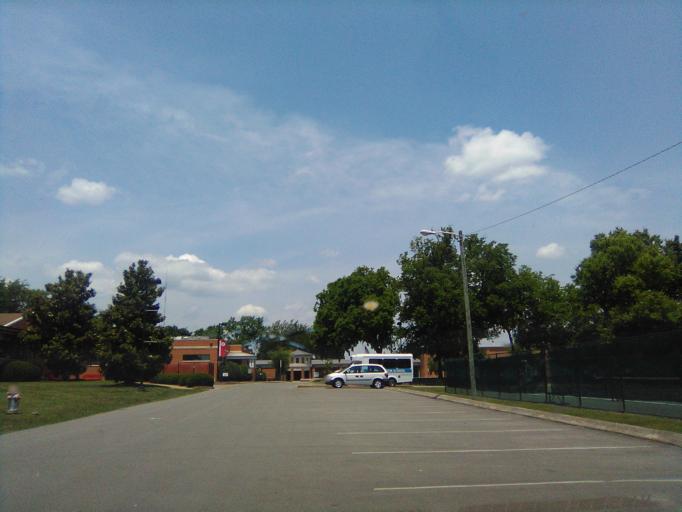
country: US
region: Tennessee
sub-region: Davidson County
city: Belle Meade
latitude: 36.1326
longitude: -86.8414
